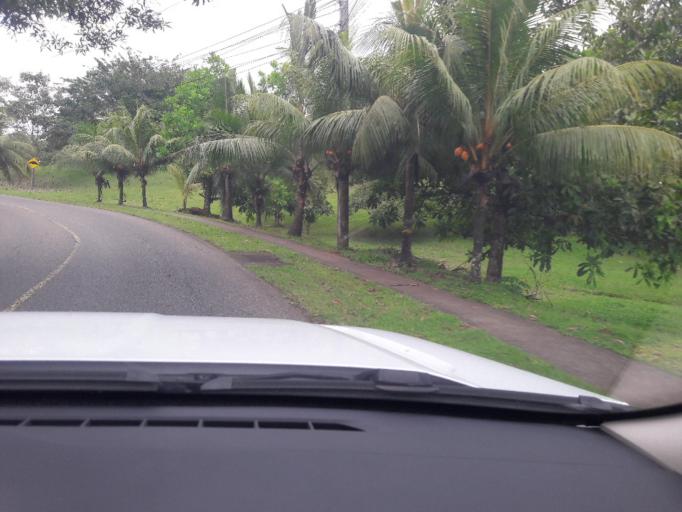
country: PA
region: Panama
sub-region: Distrito de Panama
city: Ancon
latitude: 9.0065
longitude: -79.5728
